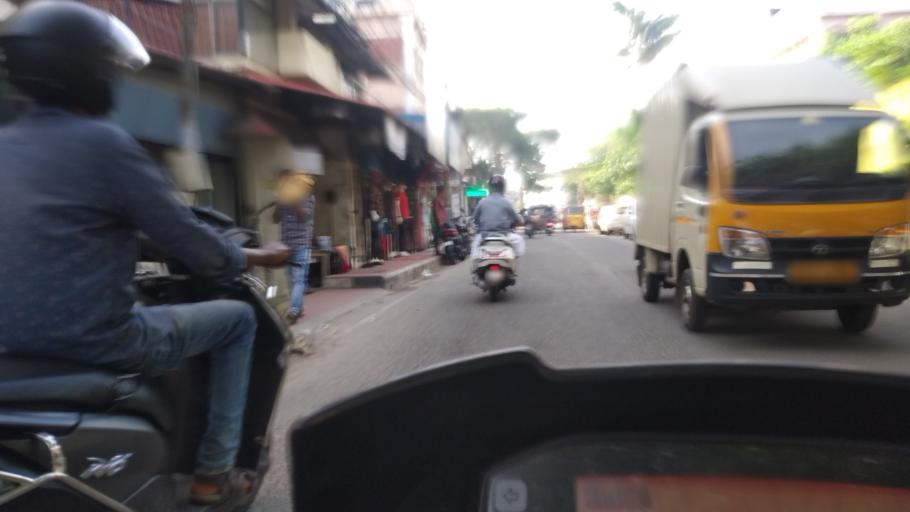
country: IN
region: Kerala
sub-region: Ernakulam
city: Elur
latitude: 10.0029
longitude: 76.2956
